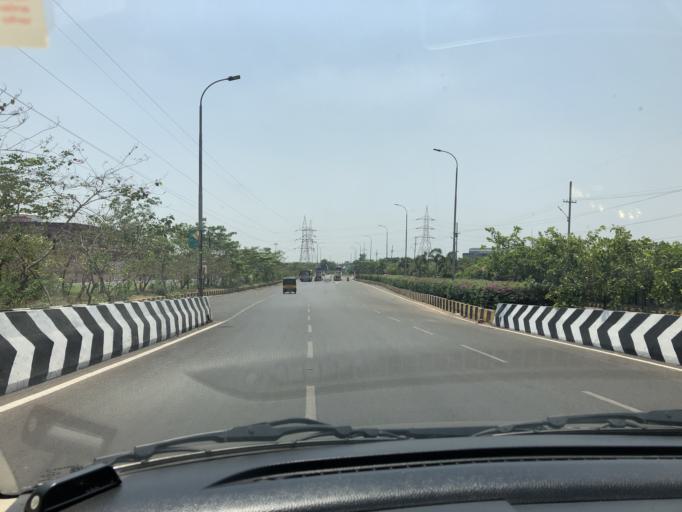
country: IN
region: Andhra Pradesh
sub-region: Vishakhapatnam
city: Gajuwaka
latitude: 17.7155
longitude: 83.2688
